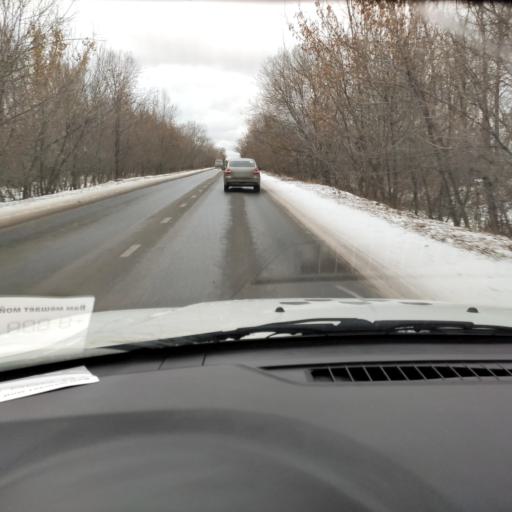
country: RU
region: Samara
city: Tol'yatti
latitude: 53.5482
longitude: 49.3936
